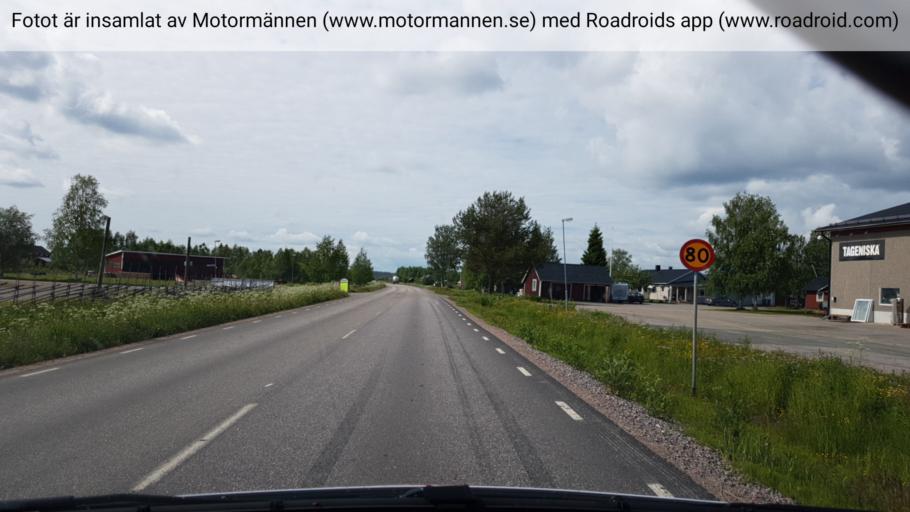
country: FI
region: Lapland
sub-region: Torniolaakso
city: Pello
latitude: 66.5602
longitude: 23.8349
